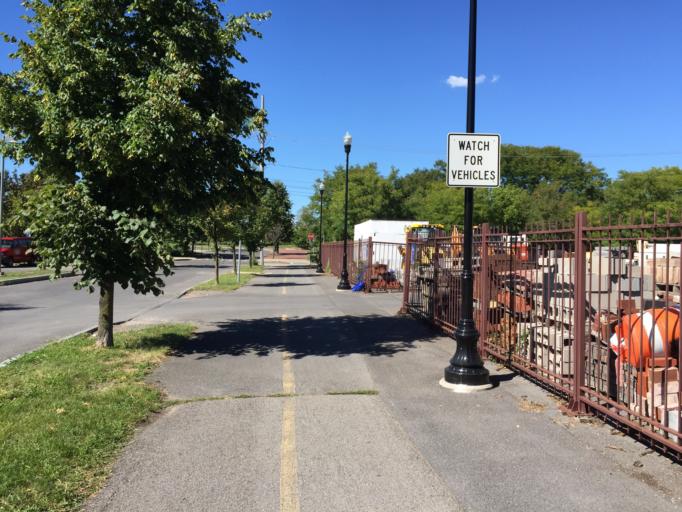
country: US
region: New York
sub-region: Onondaga County
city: Syracuse
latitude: 43.0585
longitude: -76.1648
